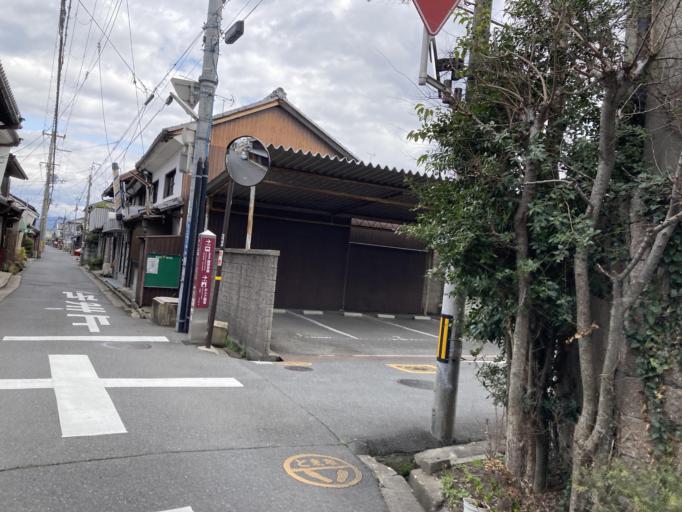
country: JP
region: Nara
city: Kashihara-shi
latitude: 34.5110
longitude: 135.7957
